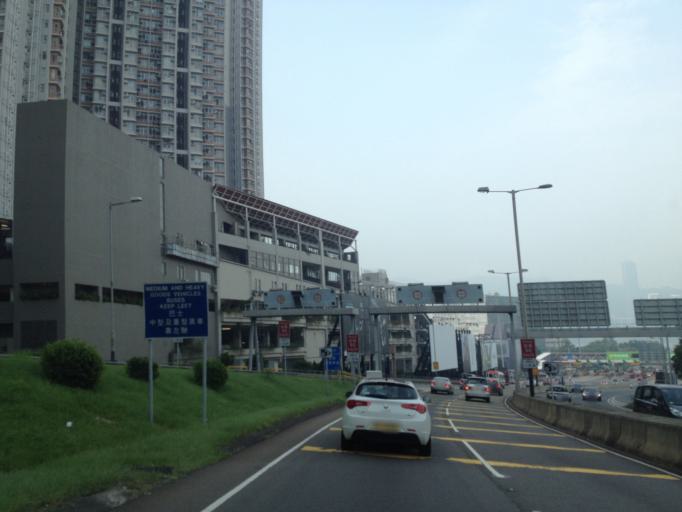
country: HK
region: Kowloon City
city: Kowloon
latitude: 22.3022
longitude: 114.2352
